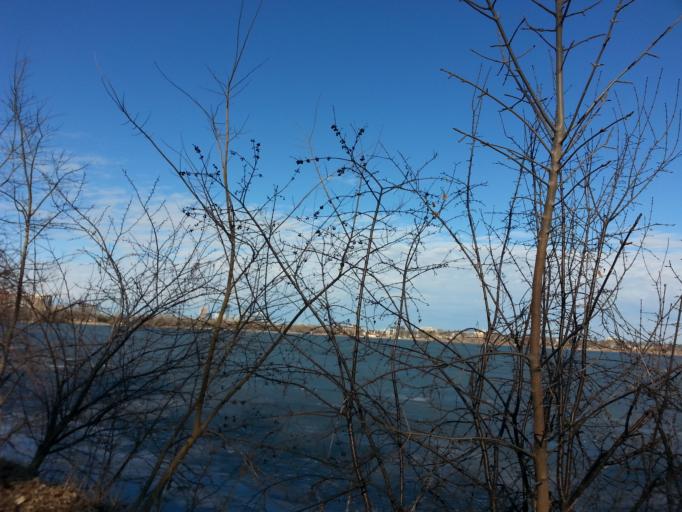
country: US
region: Minnesota
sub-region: Hennepin County
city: Saint Louis Park
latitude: 44.9427
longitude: -93.3201
